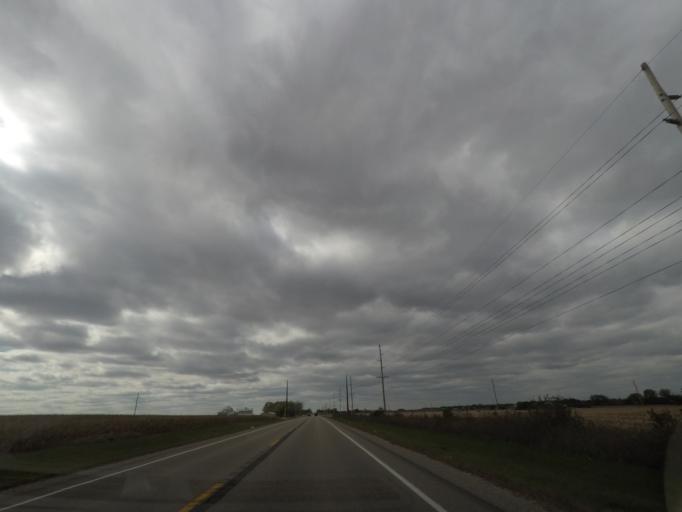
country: US
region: Iowa
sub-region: Story County
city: Huxley
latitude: 41.8778
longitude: -93.5570
